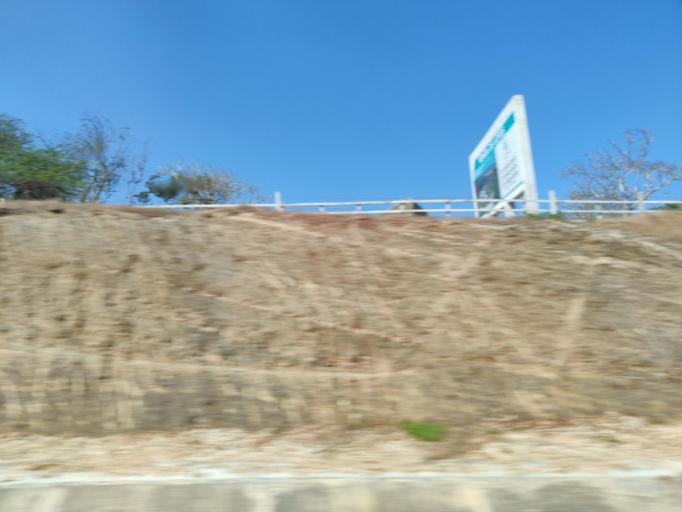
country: CO
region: Atlantico
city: Puerto Colombia
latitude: 10.9520
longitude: -75.0040
